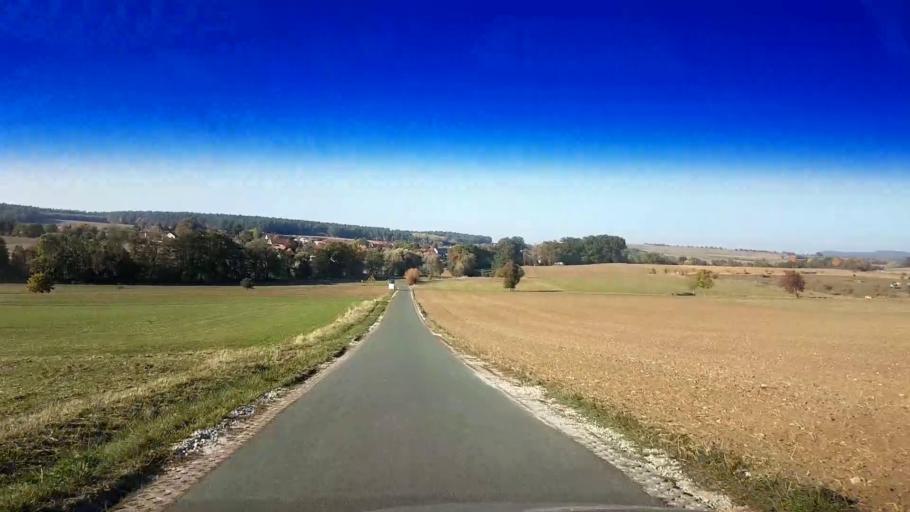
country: DE
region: Bavaria
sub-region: Upper Franconia
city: Strullendorf
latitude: 49.8594
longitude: 10.9992
